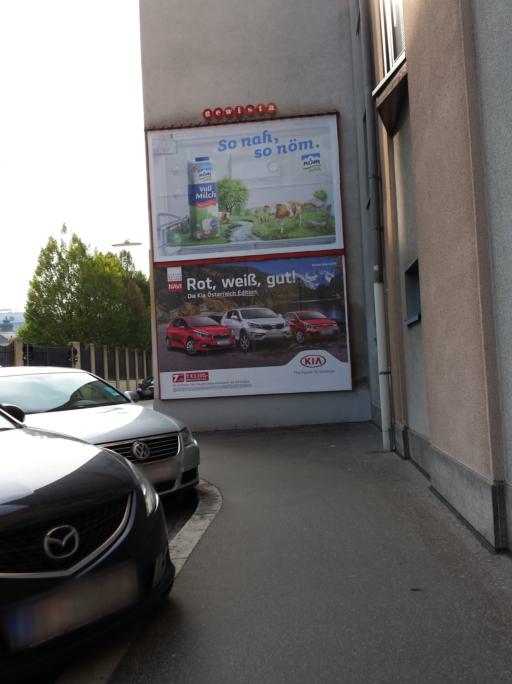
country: AT
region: Vienna
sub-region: Wien Stadt
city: Vienna
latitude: 48.1967
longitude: 16.3894
